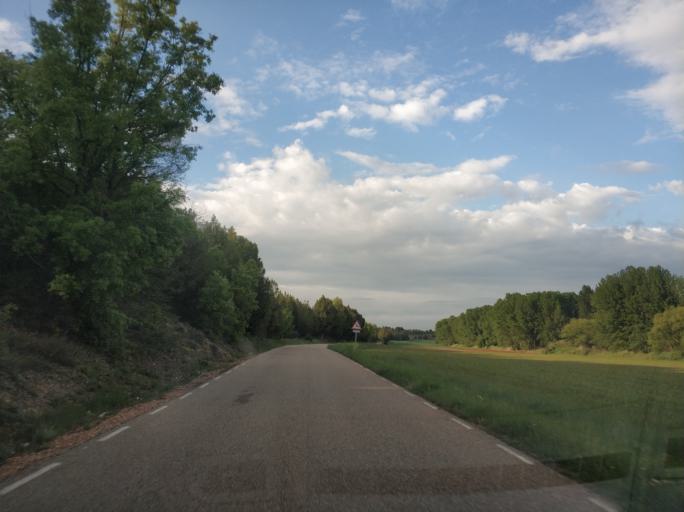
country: ES
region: Castille and Leon
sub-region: Provincia de Burgos
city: Brazacorta
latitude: 41.7041
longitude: -3.3926
